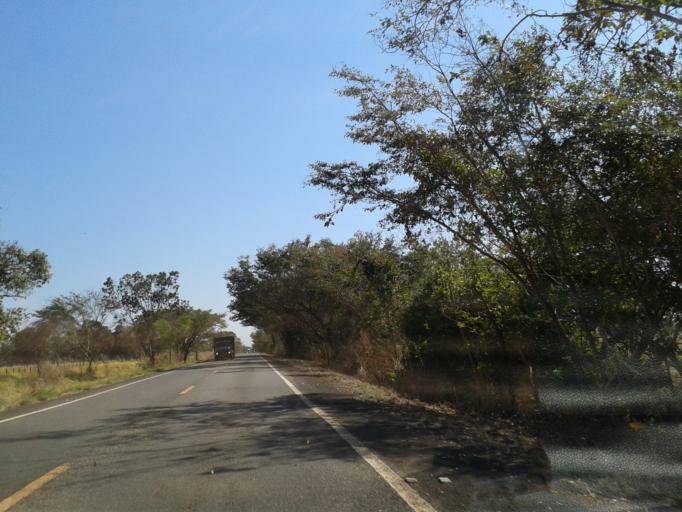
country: BR
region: Goias
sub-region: Sao Miguel Do Araguaia
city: Sao Miguel do Araguaia
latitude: -13.9237
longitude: -50.3222
